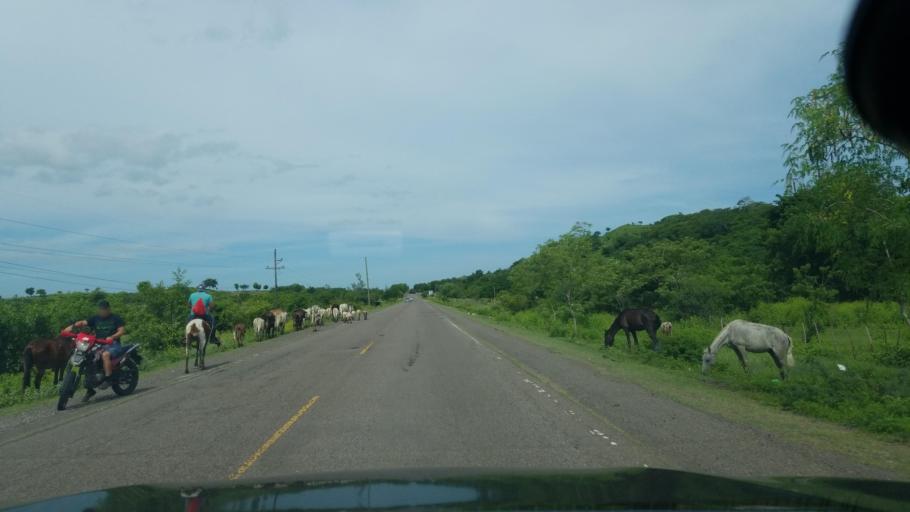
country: HN
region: Choluteca
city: Santa Ana de Yusguare
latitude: 13.3615
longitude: -87.0901
